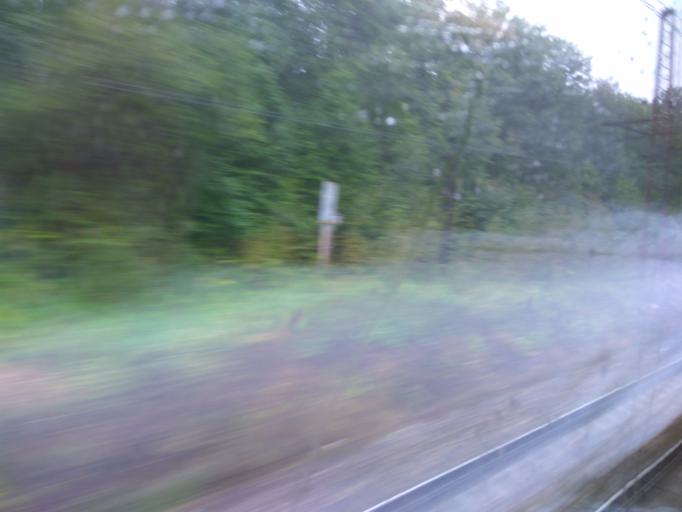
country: RU
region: Moskovskaya
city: Zhilevo
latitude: 55.0250
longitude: 38.0107
